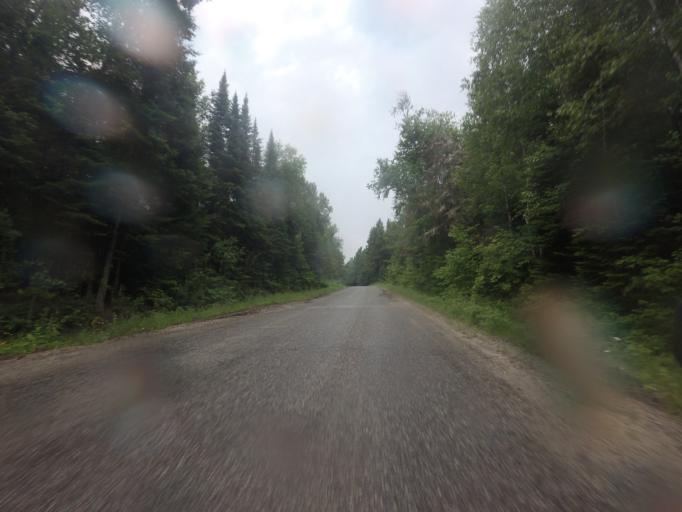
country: CA
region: Quebec
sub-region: Outaouais
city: Maniwaki
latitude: 46.4324
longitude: -75.9465
